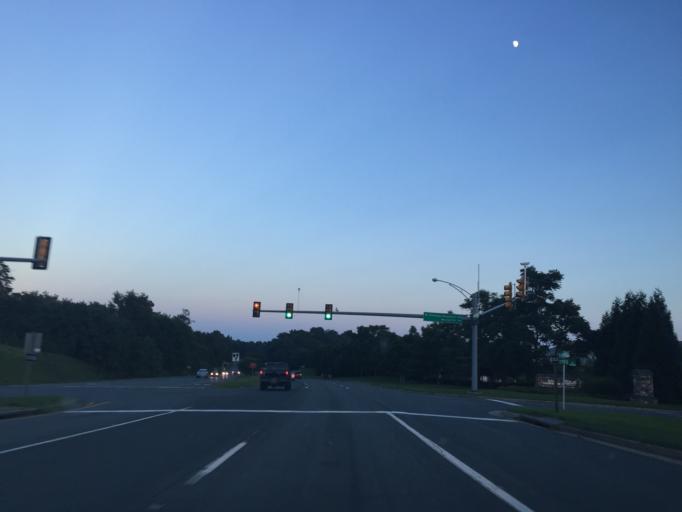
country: US
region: Virginia
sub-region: City of Charlottesville
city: Charlottesville
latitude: 38.0269
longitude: -78.4393
